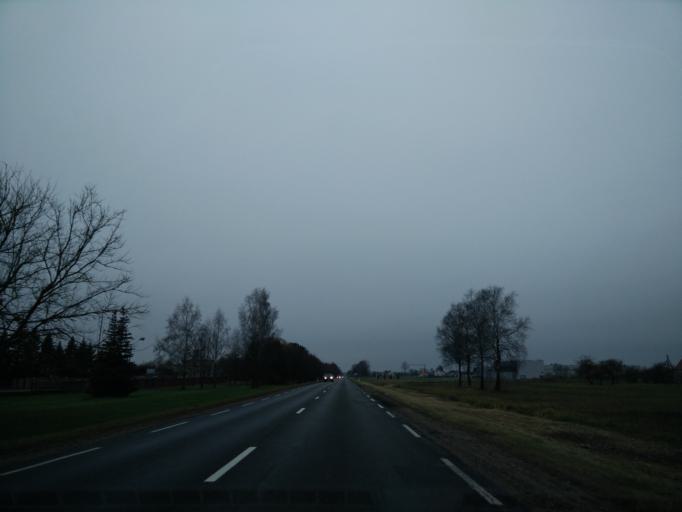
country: LT
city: Ariogala
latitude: 55.2597
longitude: 23.4940
